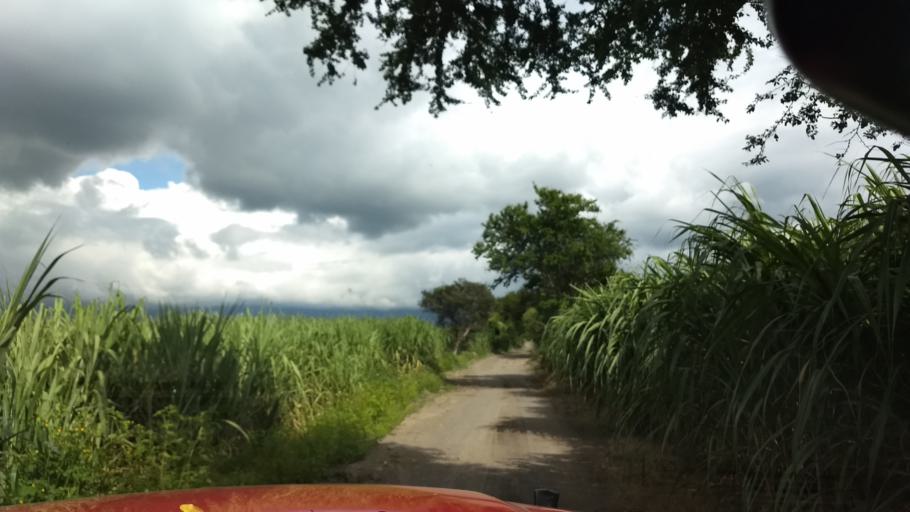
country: MX
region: Colima
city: Suchitlan
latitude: 19.4610
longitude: -103.7617
